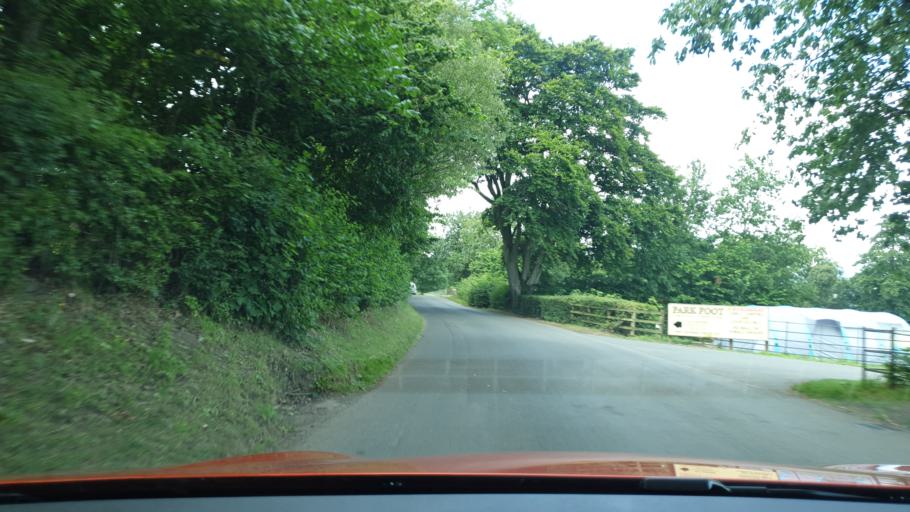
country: GB
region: England
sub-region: Cumbria
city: Penrith
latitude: 54.6052
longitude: -2.8226
